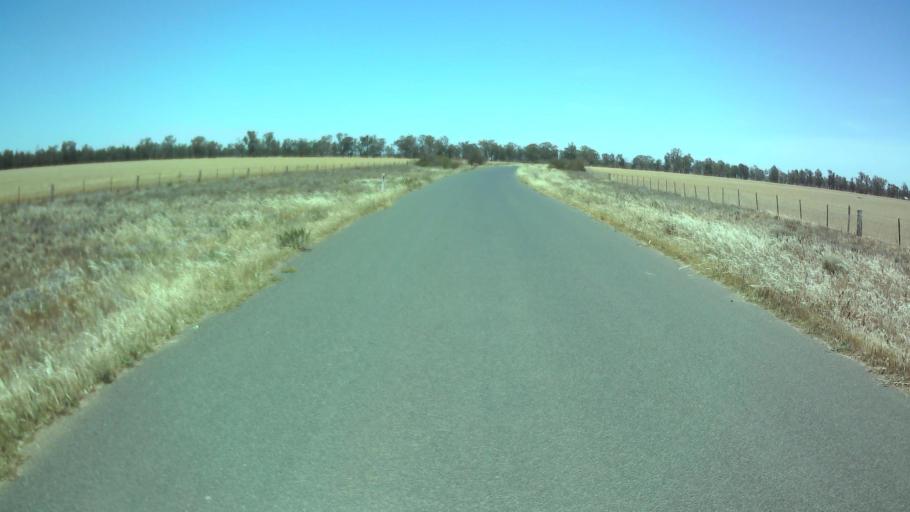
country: AU
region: New South Wales
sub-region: Weddin
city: Grenfell
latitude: -34.0693
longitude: 147.7770
